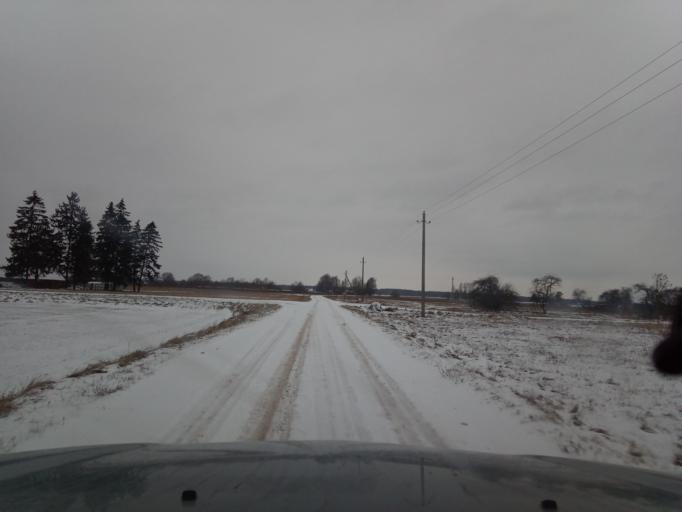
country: LT
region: Vilnius County
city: Ukmerge
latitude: 55.4828
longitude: 24.6027
